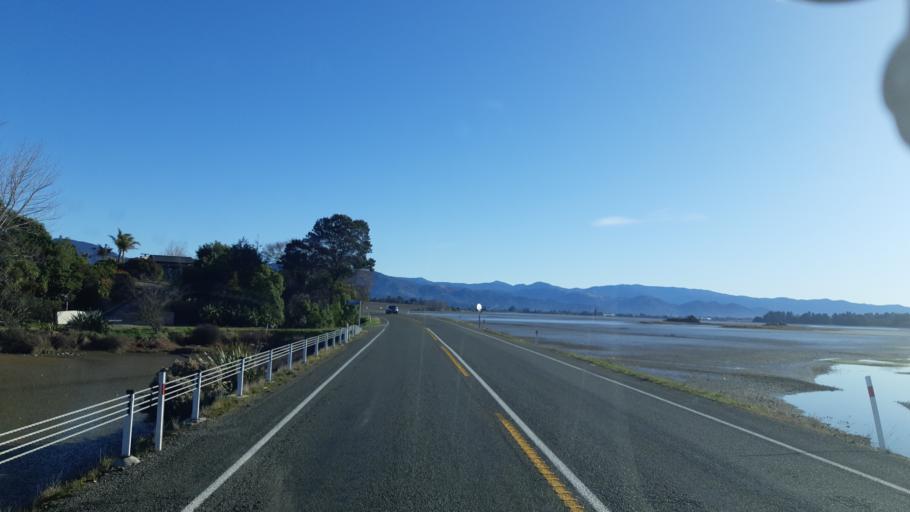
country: NZ
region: Tasman
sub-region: Tasman District
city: Motueka
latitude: -41.1647
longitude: 173.0281
